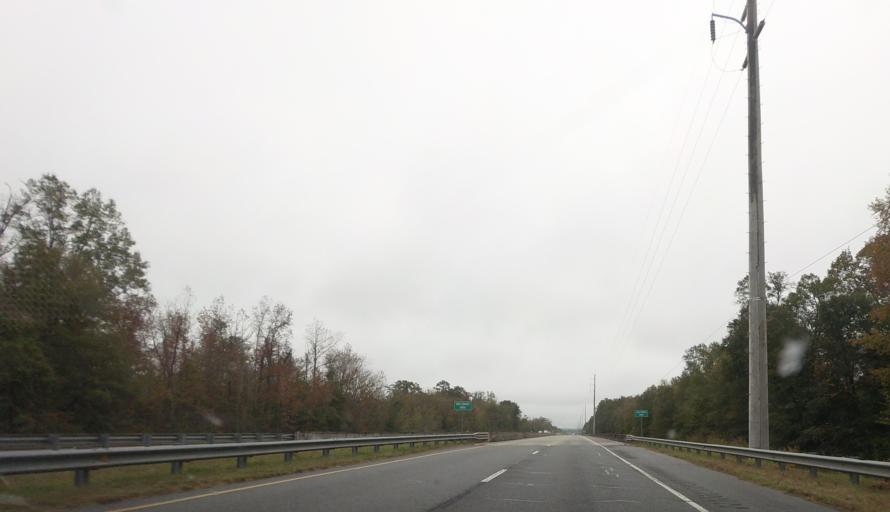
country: US
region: Georgia
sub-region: Taylor County
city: Reynolds
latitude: 32.5504
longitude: -84.0481
